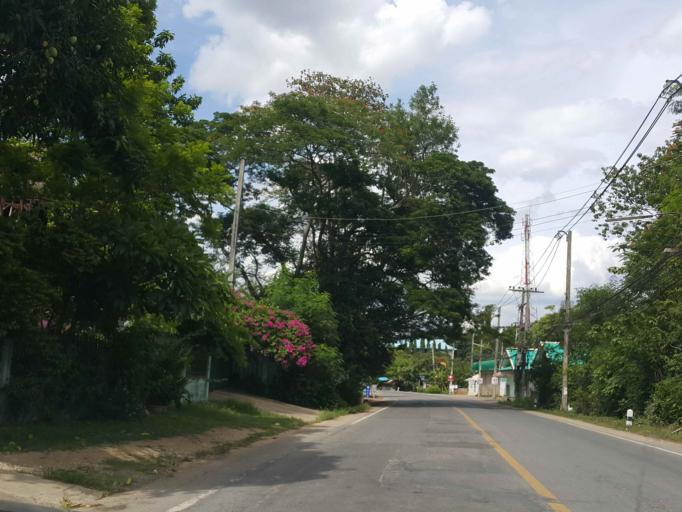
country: TH
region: Chiang Mai
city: Chiang Mai
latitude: 18.9192
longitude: 98.9154
